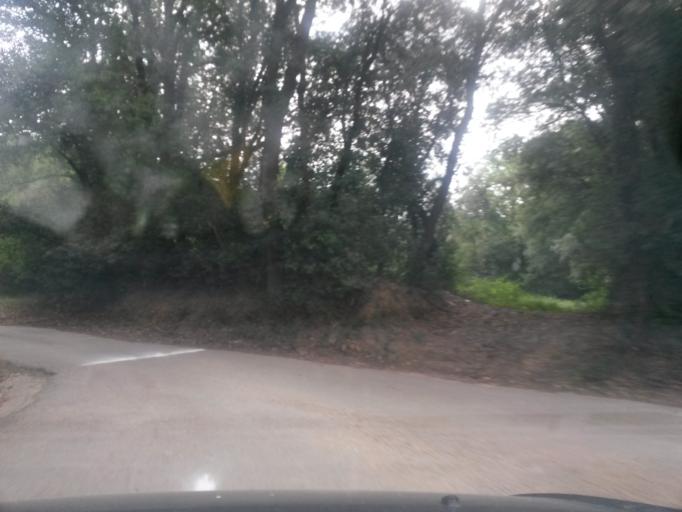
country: ES
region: Catalonia
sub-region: Provincia de Girona
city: Sant Gregori
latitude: 41.9750
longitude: 2.7048
